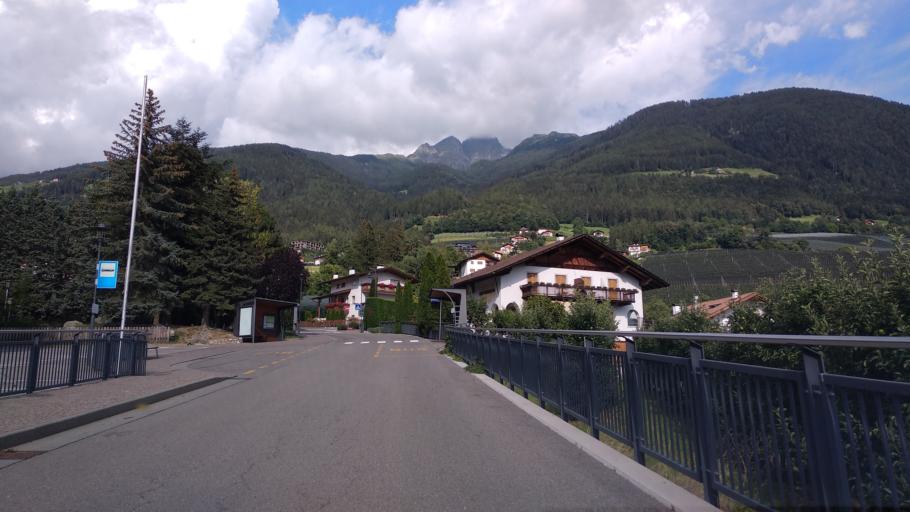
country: IT
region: Trentino-Alto Adige
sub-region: Bolzano
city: Scena - Schenna
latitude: 46.6929
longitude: 11.1886
